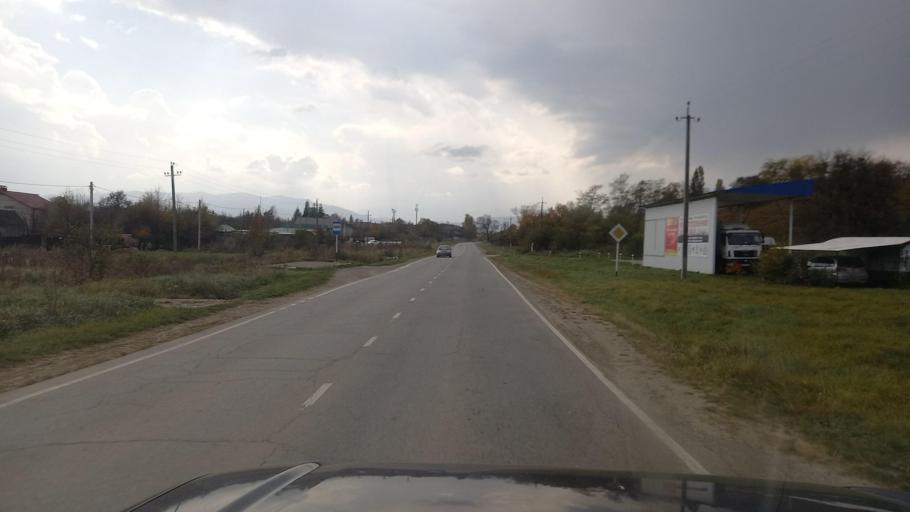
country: RU
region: Krasnodarskiy
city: Psebay
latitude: 44.1431
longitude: 40.8237
